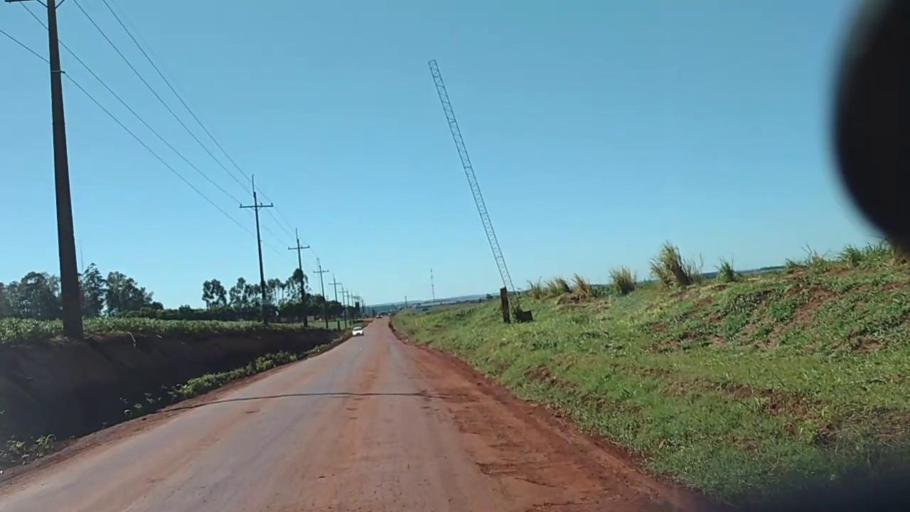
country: PY
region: Alto Parana
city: Naranjal
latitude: -25.9751
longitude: -55.2165
